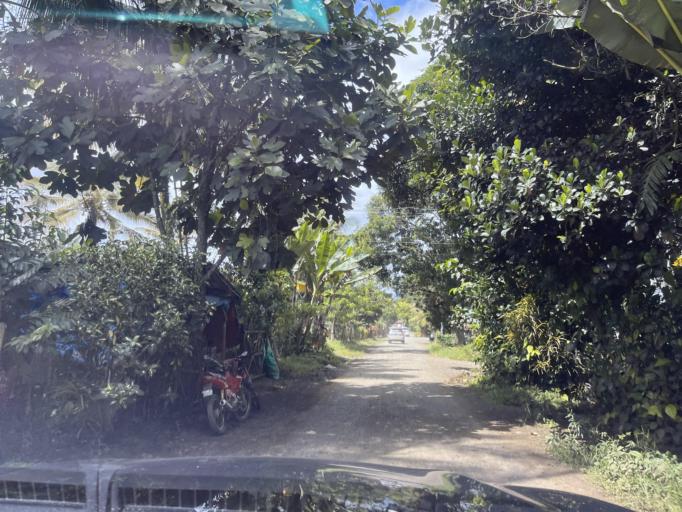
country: PH
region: Northern Mindanao
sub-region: Province of Bukidnon
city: Impalutao
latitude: 8.2715
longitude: 125.0181
